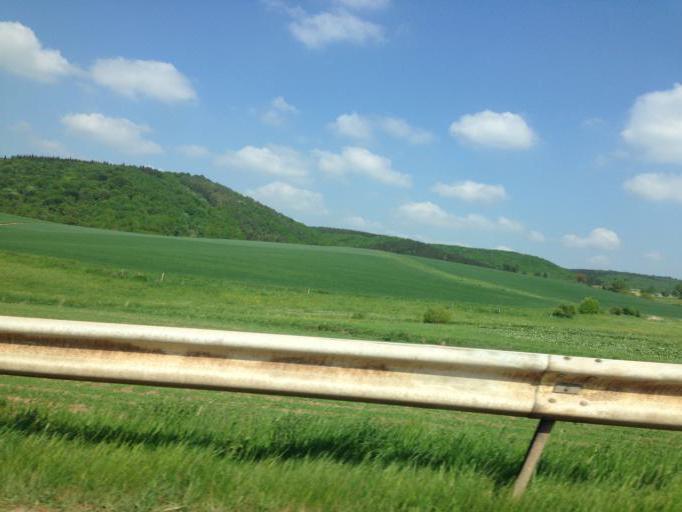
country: DE
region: North Rhine-Westphalia
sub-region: Regierungsbezirk Koln
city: Bad Munstereifel
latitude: 50.5518
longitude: 6.7220
